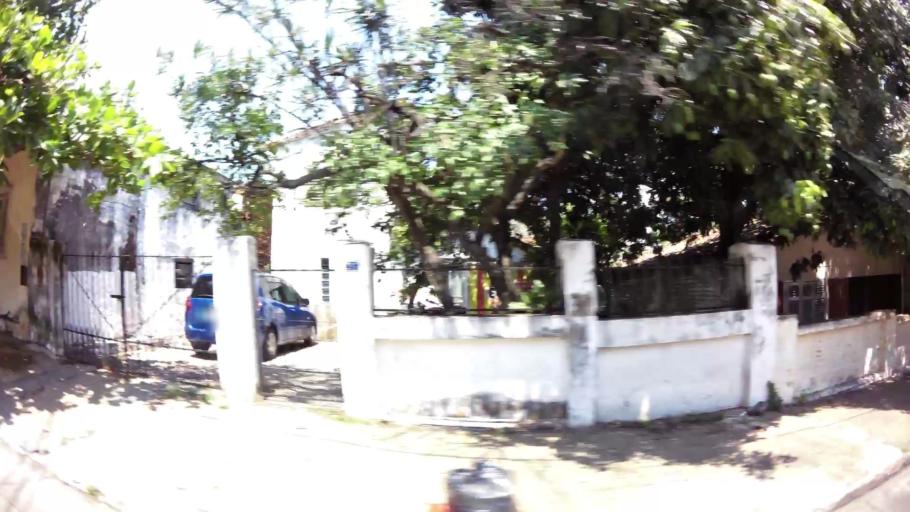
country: PY
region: Asuncion
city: Asuncion
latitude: -25.2978
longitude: -57.6532
